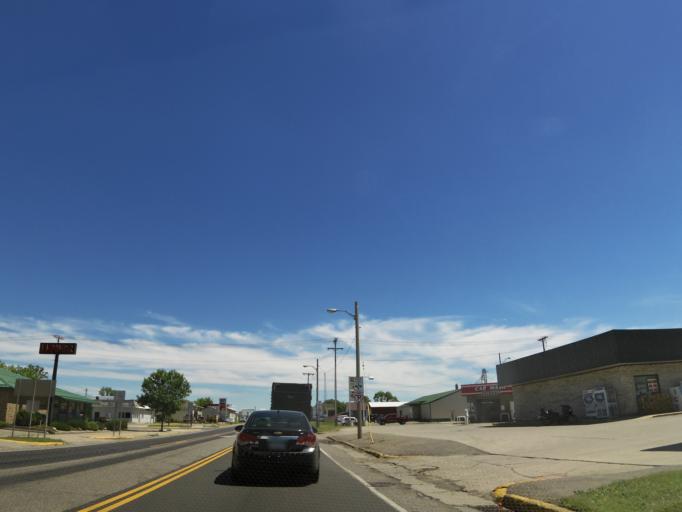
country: US
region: Minnesota
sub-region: Wadena County
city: Wadena
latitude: 46.4422
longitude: -95.1358
